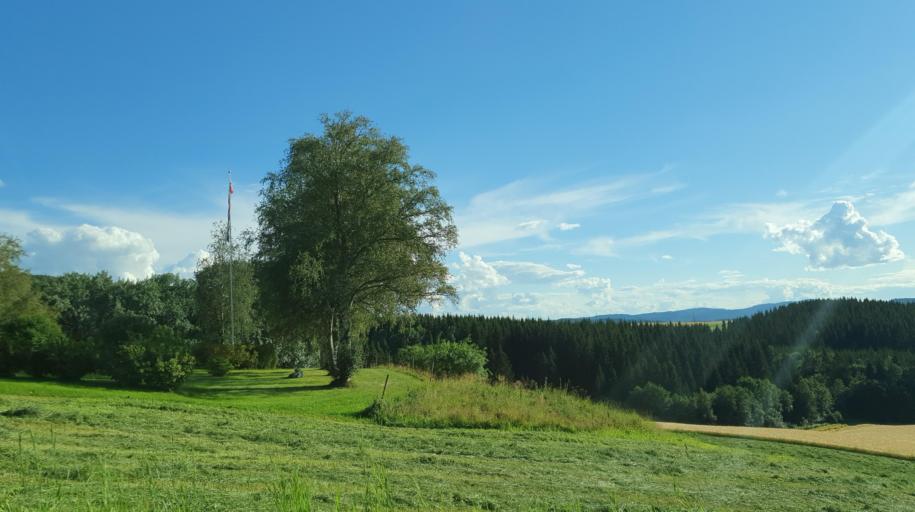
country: NO
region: Nord-Trondelag
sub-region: Levanger
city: Skogn
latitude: 63.6981
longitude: 11.2556
